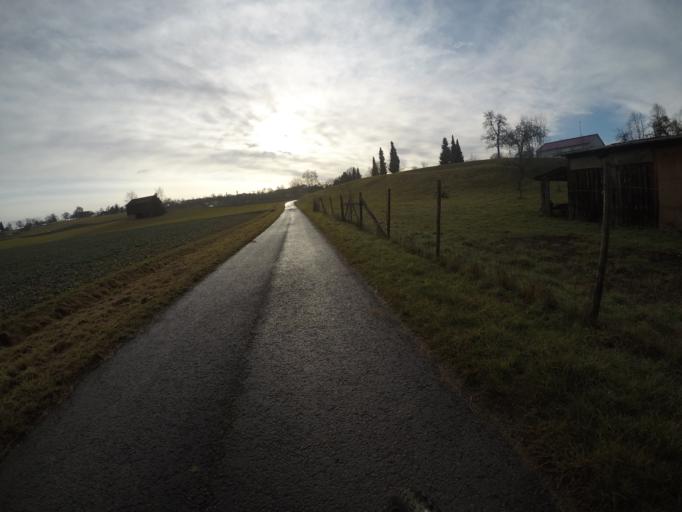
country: DE
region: Baden-Wuerttemberg
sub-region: Regierungsbezirk Stuttgart
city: Deckenpfronn
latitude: 48.6587
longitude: 8.8243
